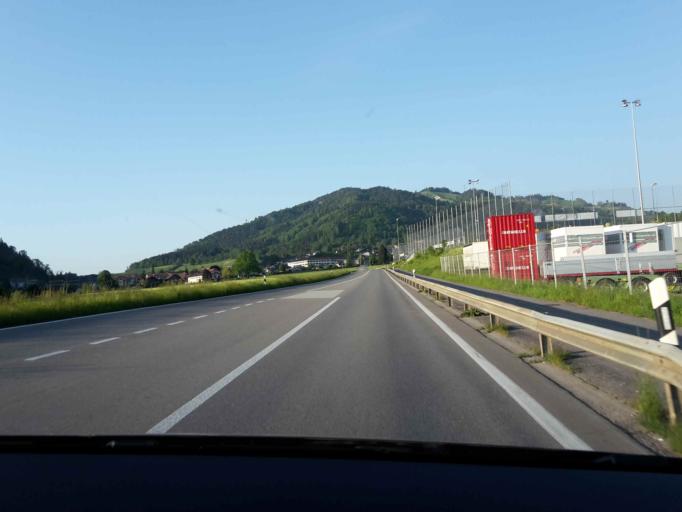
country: CH
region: Lucerne
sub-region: Entlebuch District
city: Oberdiessbach
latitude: 46.8316
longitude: 7.6143
